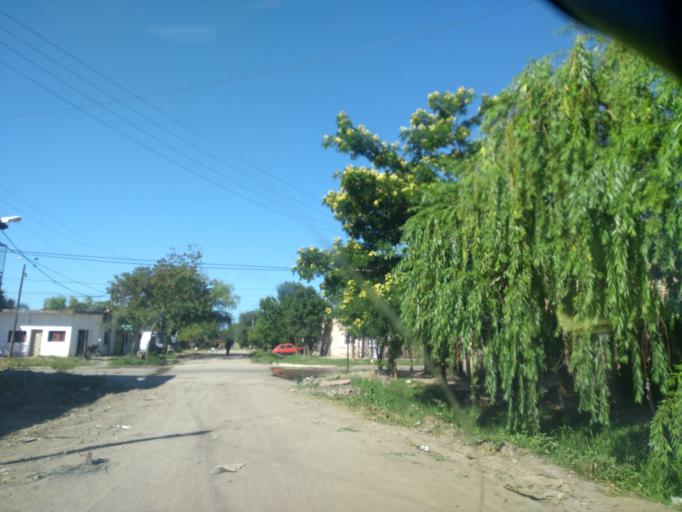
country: AR
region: Chaco
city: Resistencia
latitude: -27.4751
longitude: -58.9652
